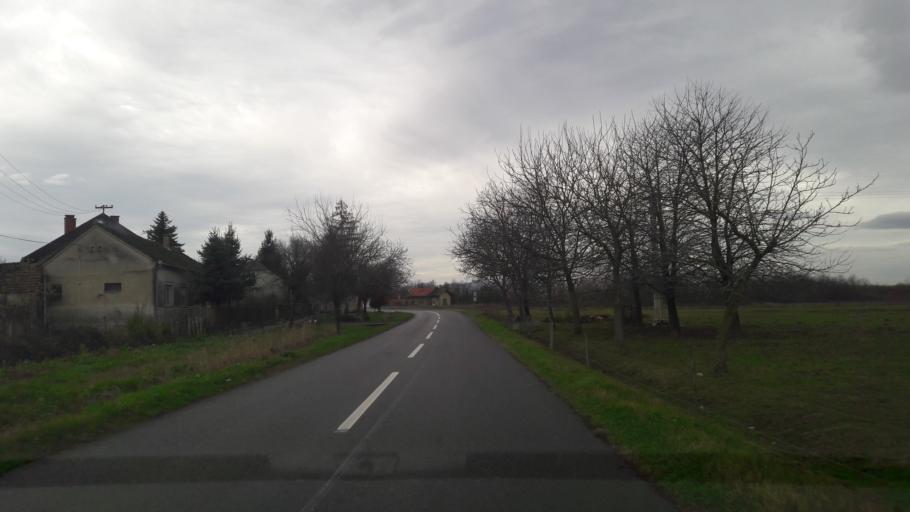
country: HR
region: Osjecko-Baranjska
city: Martin
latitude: 45.5349
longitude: 18.0628
